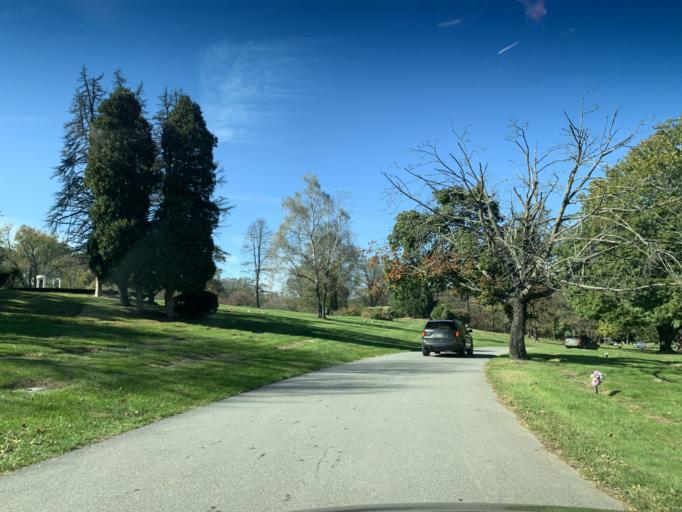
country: US
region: Pennsylvania
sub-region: Berks County
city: Mount Penn
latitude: 40.3121
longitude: -75.8900
